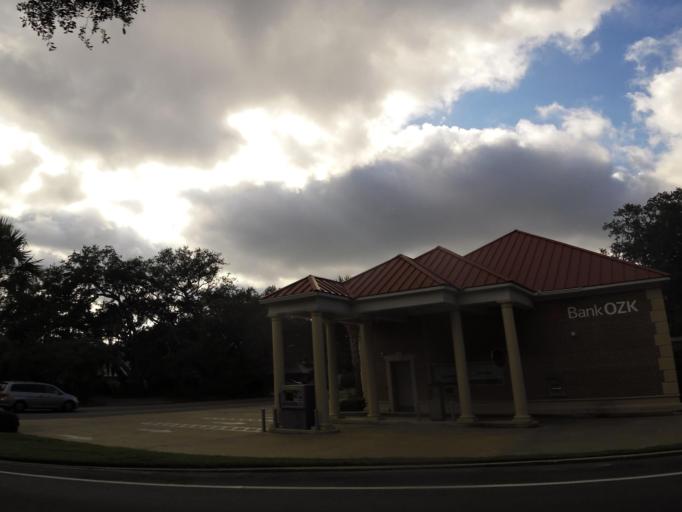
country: US
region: Georgia
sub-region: Glynn County
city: Saint Simon Mills
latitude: 31.1649
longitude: -81.3865
